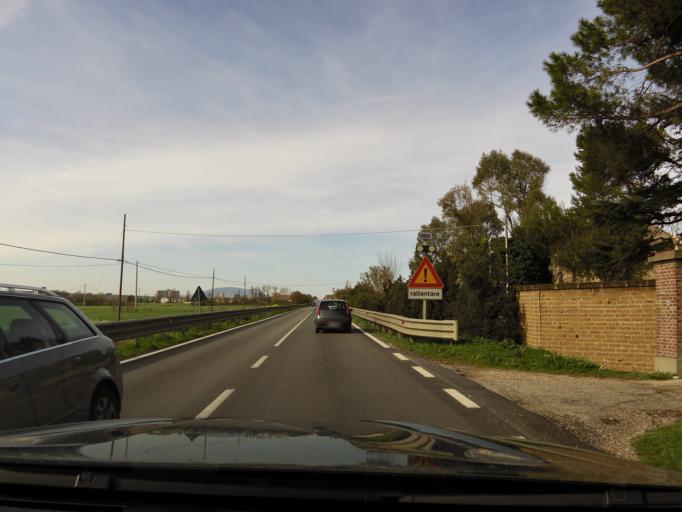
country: IT
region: The Marches
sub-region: Provincia di Macerata
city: Porto Recanati
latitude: 43.3962
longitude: 13.6793
